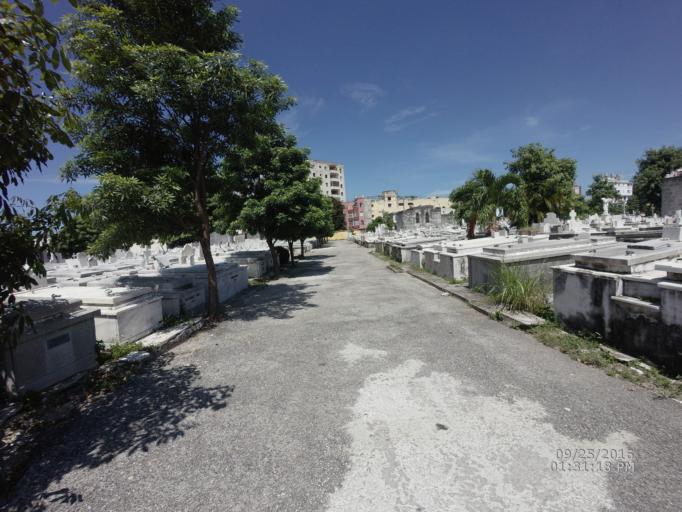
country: CU
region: La Habana
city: Havana
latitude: 23.1253
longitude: -82.4018
